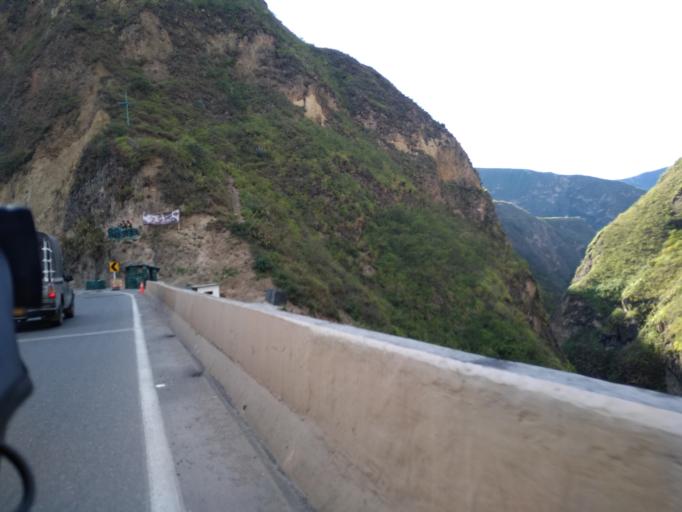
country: CO
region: Narino
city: Imues
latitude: 1.0568
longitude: -77.4483
